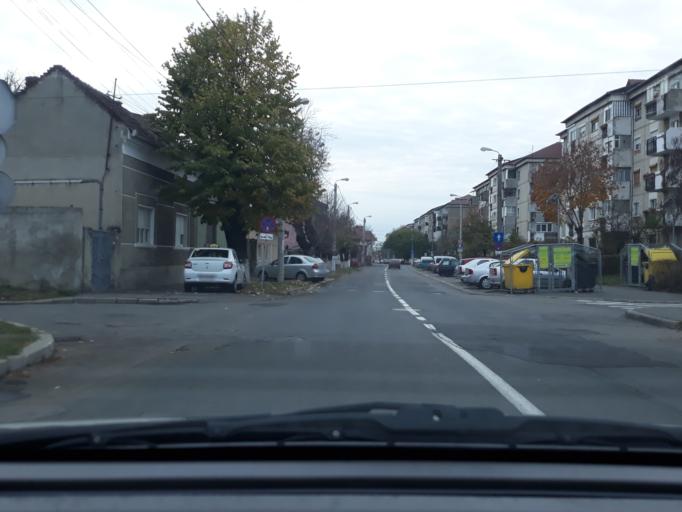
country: RO
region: Bihor
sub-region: Comuna Biharea
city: Oradea
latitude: 47.0480
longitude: 21.9551
